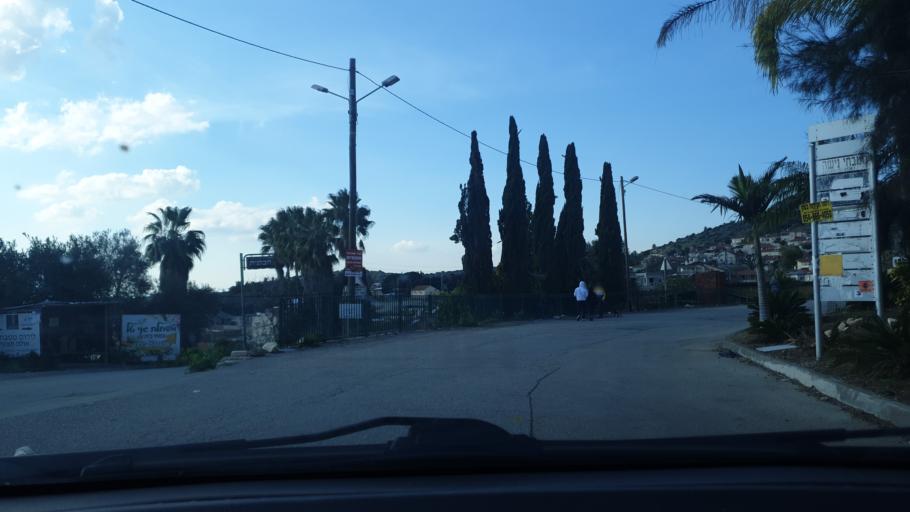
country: IL
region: Jerusalem
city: Bet Shemesh
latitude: 31.7069
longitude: 34.9484
